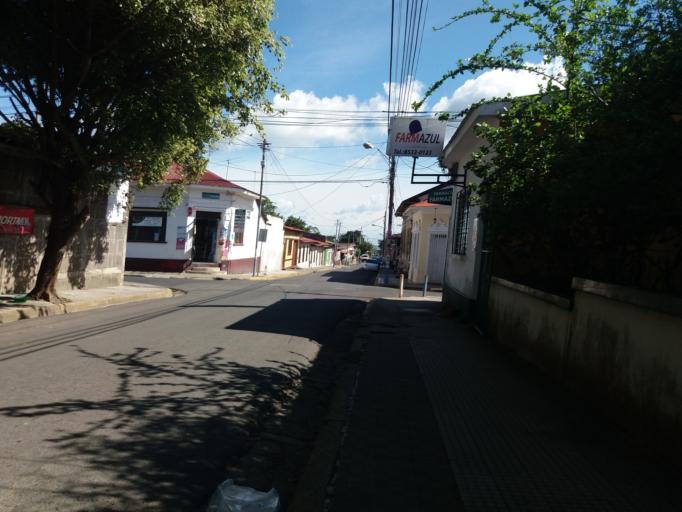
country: NI
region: Carazo
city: Jinotepe
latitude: 11.8462
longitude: -86.1983
